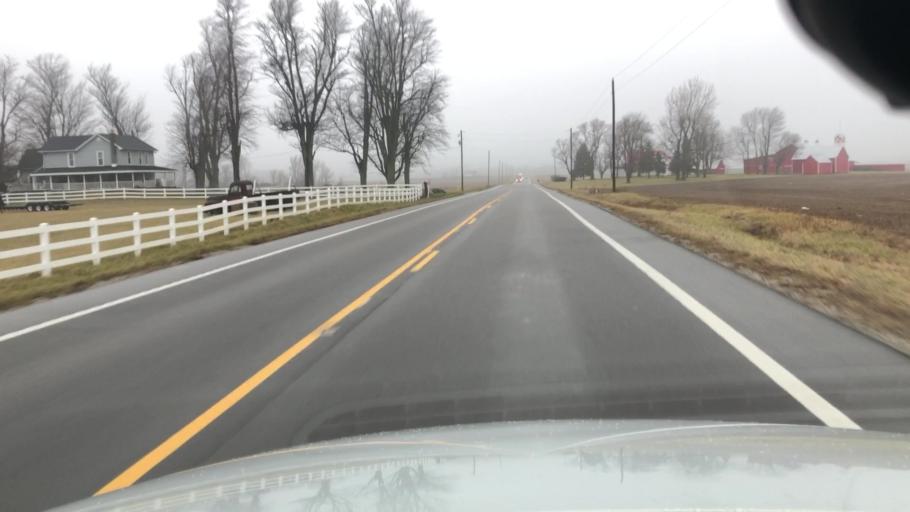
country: US
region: Ohio
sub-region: Logan County
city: Lakeview
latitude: 40.6354
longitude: -83.9204
